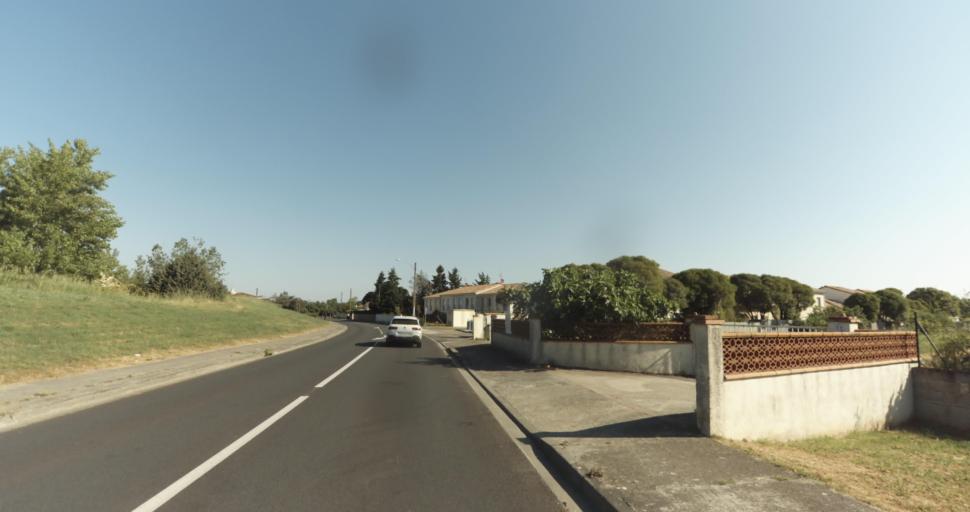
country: FR
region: Midi-Pyrenees
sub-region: Departement de la Haute-Garonne
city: Plaisance-du-Touch
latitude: 43.5574
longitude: 1.3030
